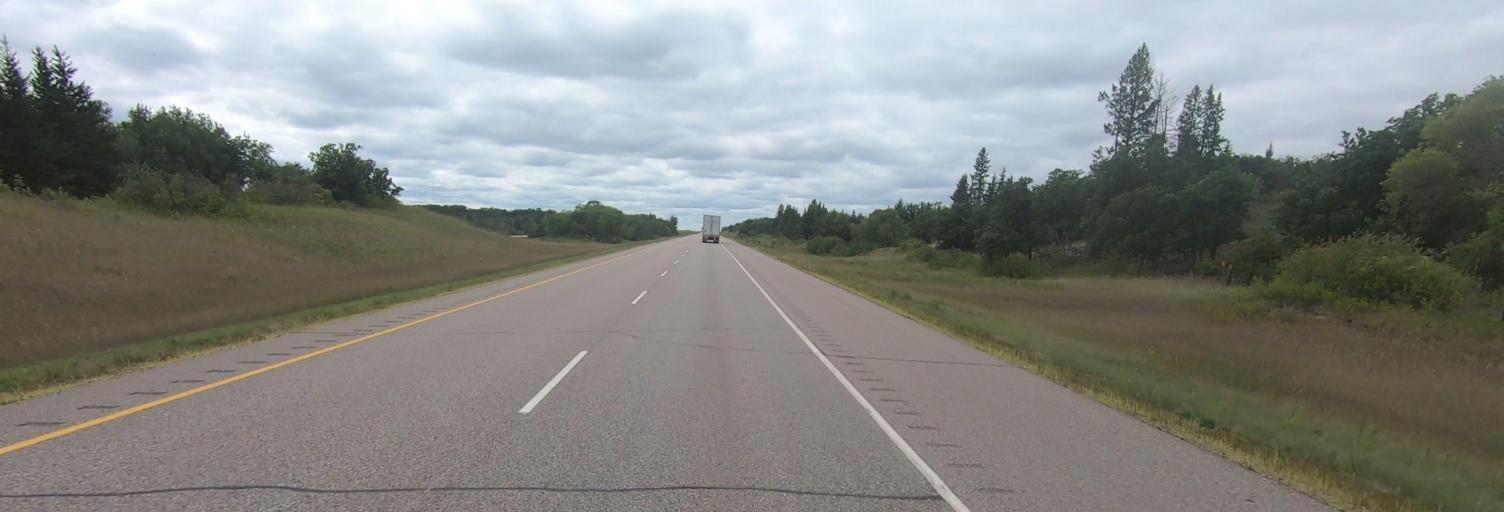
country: CA
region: Manitoba
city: Carberry
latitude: 49.9015
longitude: -99.2605
